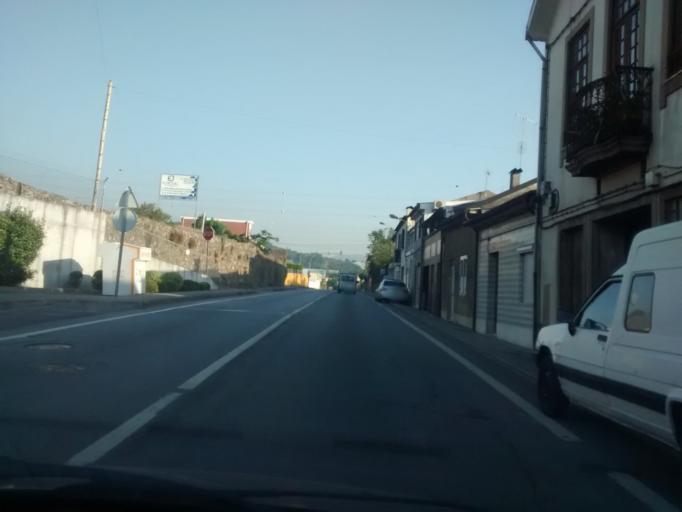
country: PT
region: Braga
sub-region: Braga
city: Braga
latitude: 41.5768
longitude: -8.4257
